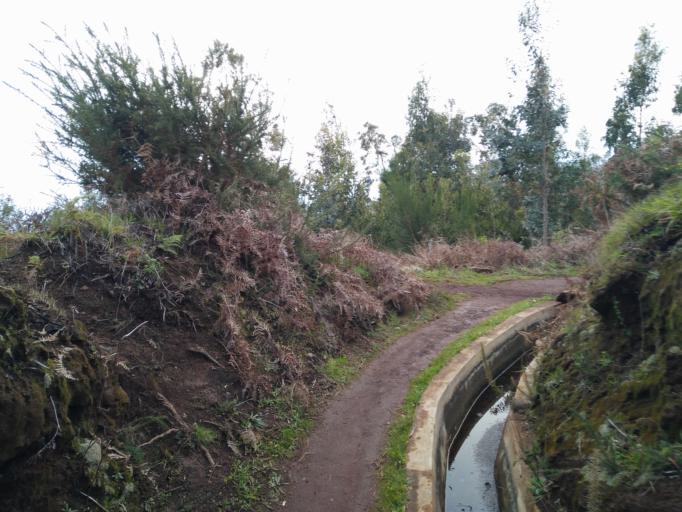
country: PT
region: Madeira
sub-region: Calheta
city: Faja da Ovelha
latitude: 32.8179
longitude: -17.2296
